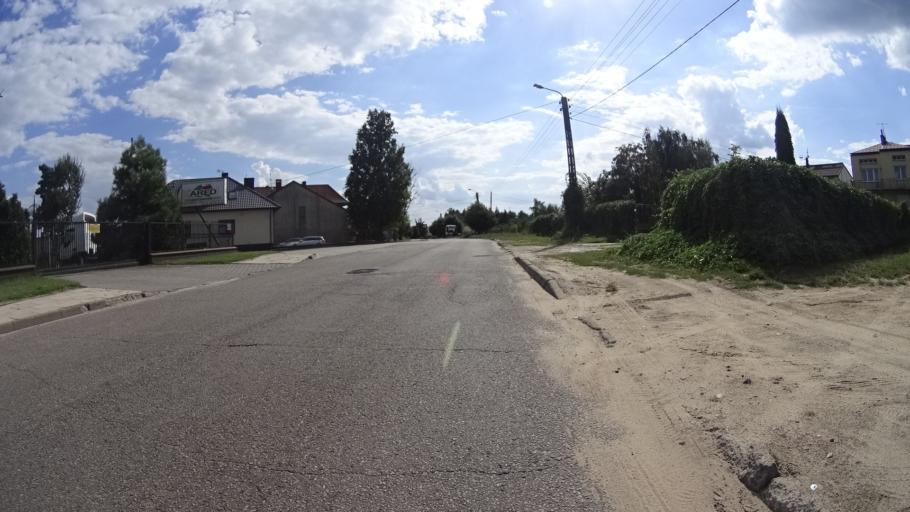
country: PL
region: Masovian Voivodeship
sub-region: Powiat grojecki
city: Mogielnica
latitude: 51.6862
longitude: 20.7182
